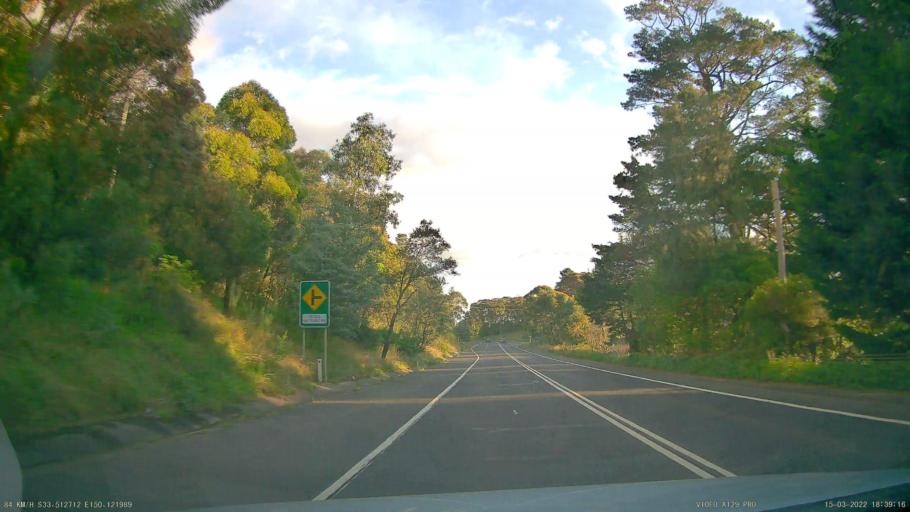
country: AU
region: New South Wales
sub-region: Lithgow
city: Bowenfels
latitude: -33.5132
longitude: 150.1219
